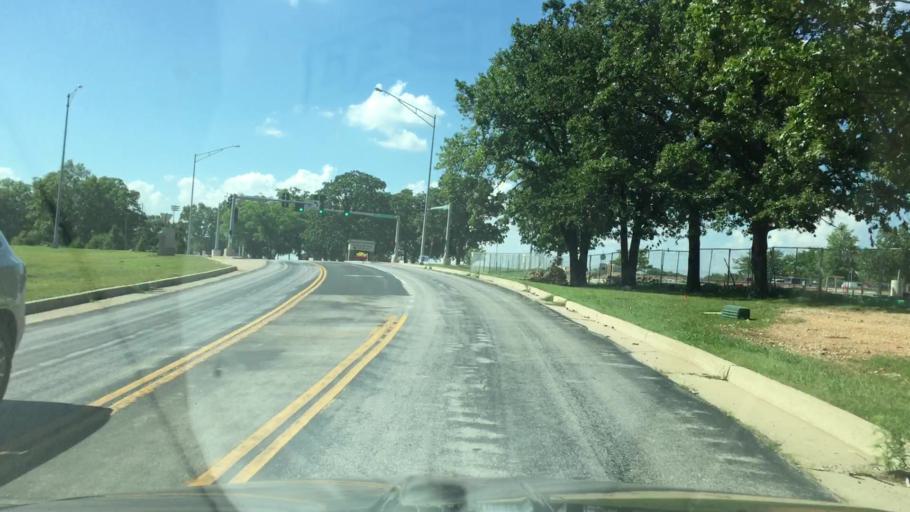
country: US
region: Missouri
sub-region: Camden County
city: Osage Beach
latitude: 38.1452
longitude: -92.5918
